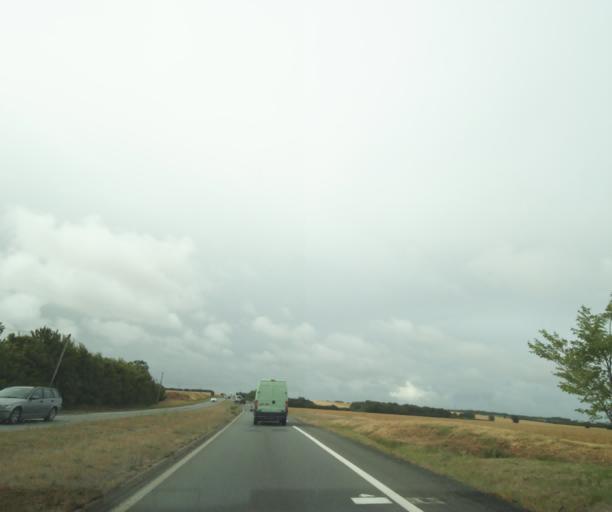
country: FR
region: Poitou-Charentes
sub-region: Departement de la Charente-Maritime
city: Marsilly
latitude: 46.2091
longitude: -1.1365
